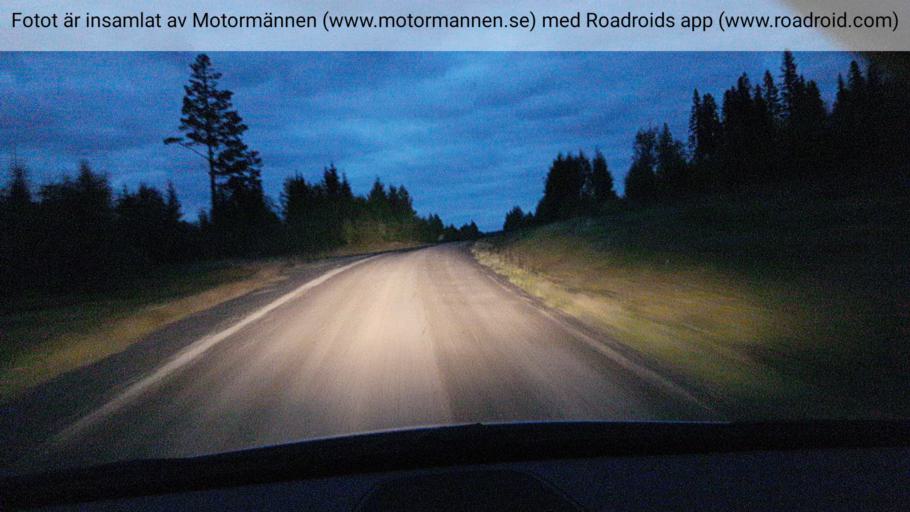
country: SE
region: Jaemtland
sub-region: Braecke Kommun
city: Braecke
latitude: 63.2535
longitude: 15.3706
